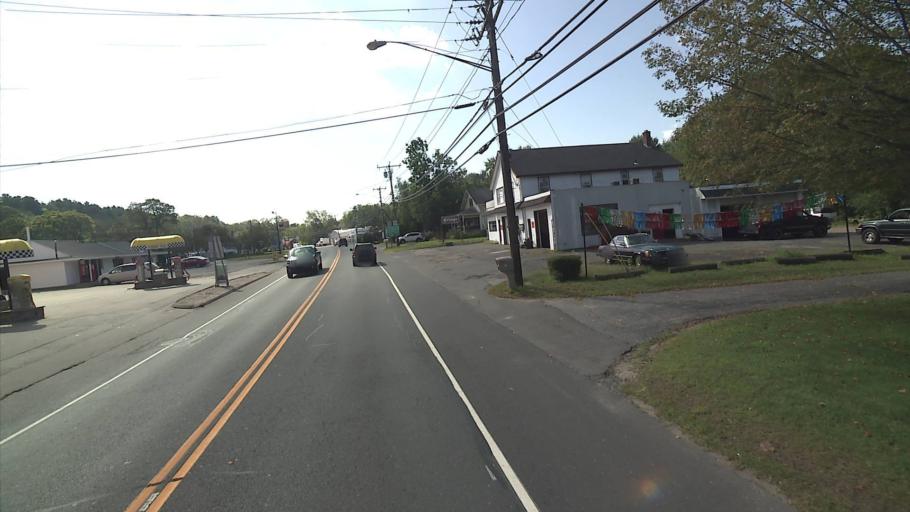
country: US
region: Connecticut
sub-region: Tolland County
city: Stafford Springs
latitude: 41.9613
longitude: -72.3149
